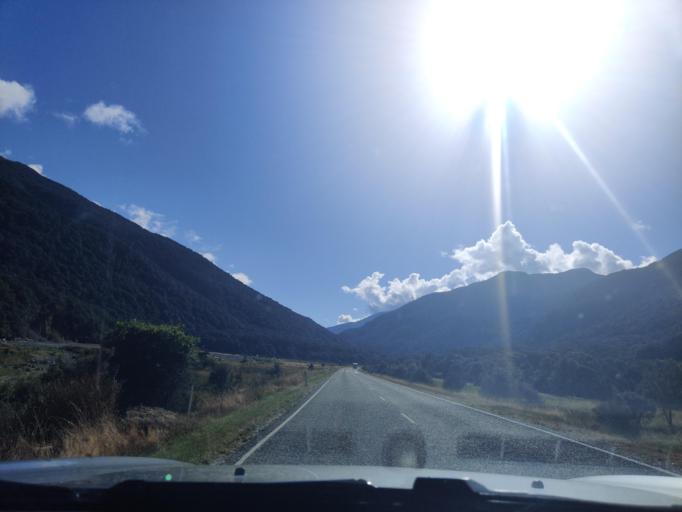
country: NZ
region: Otago
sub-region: Queenstown-Lakes District
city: Wanaka
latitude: -44.1476
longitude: 169.3189
